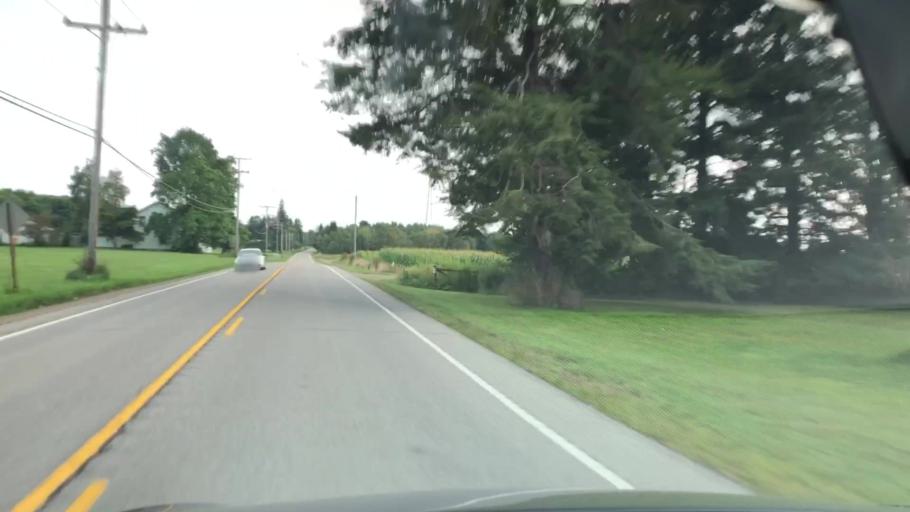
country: US
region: Pennsylvania
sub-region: Crawford County
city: Titusville
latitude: 41.5867
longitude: -79.6857
